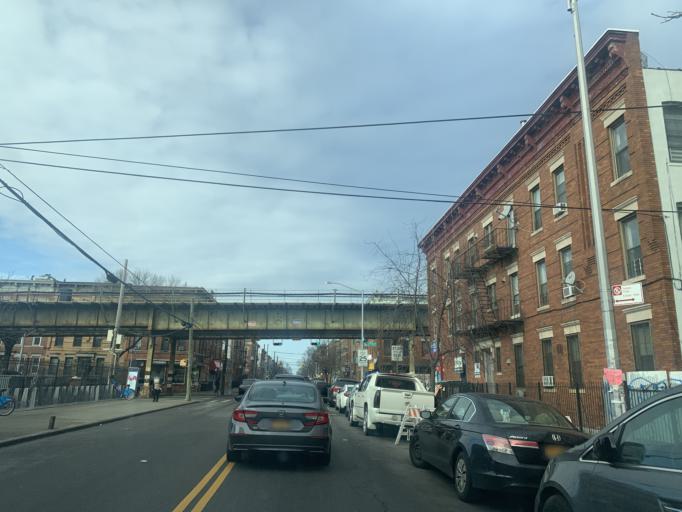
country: US
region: New York
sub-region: Kings County
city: East New York
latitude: 40.7015
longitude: -73.9084
